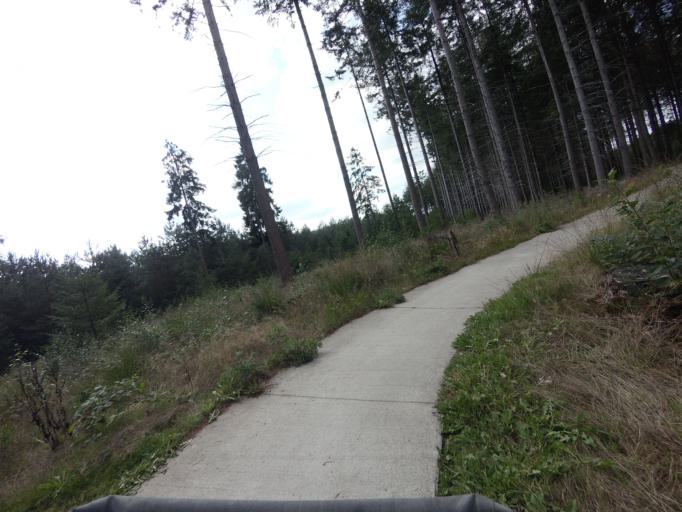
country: NL
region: Drenthe
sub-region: Gemeente Westerveld
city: Dwingeloo
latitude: 52.8371
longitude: 6.4754
